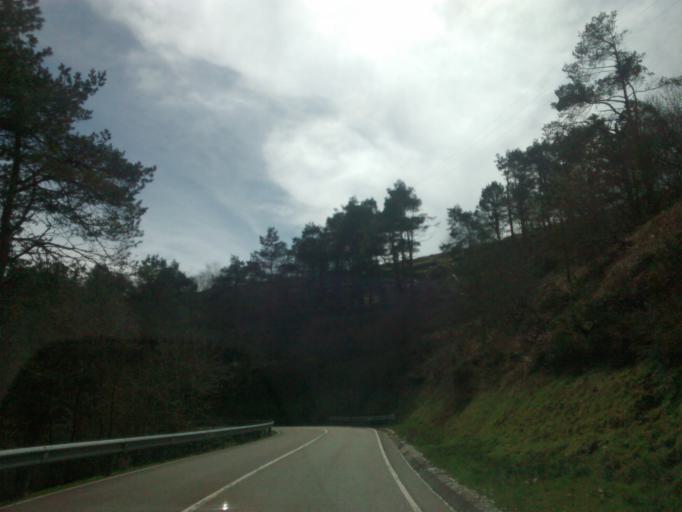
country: ES
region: Cantabria
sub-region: Provincia de Cantabria
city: Vega de Pas
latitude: 43.1797
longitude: -3.8000
